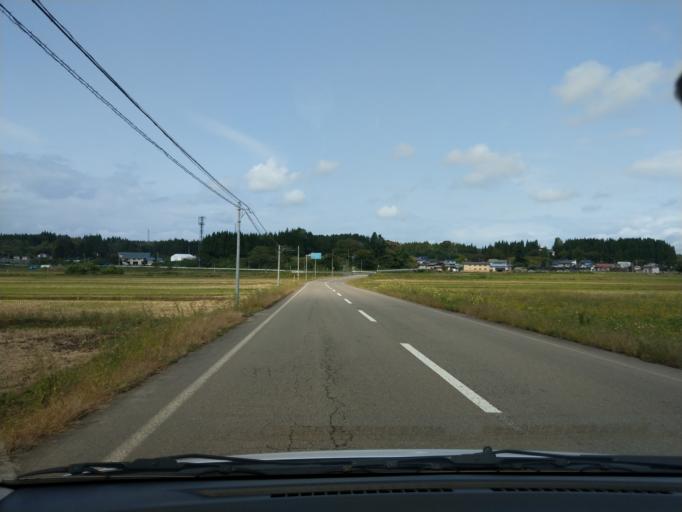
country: JP
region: Akita
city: Omagari
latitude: 39.5168
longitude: 140.3059
